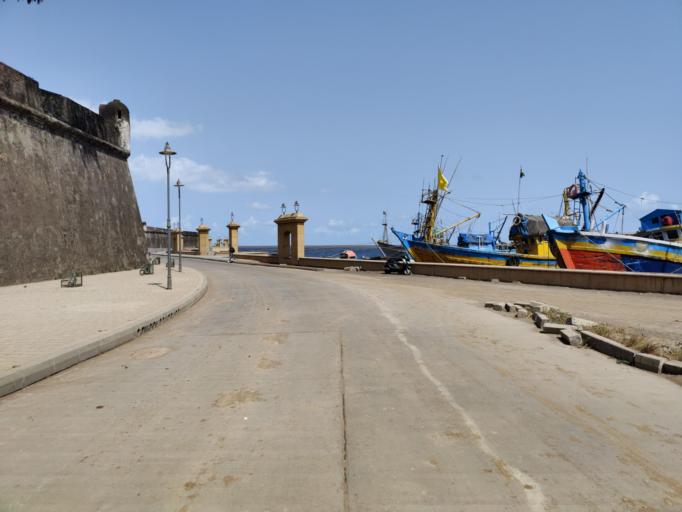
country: IN
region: Daman and Diu
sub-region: Daman District
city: Daman
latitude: 20.4103
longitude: 72.8336
